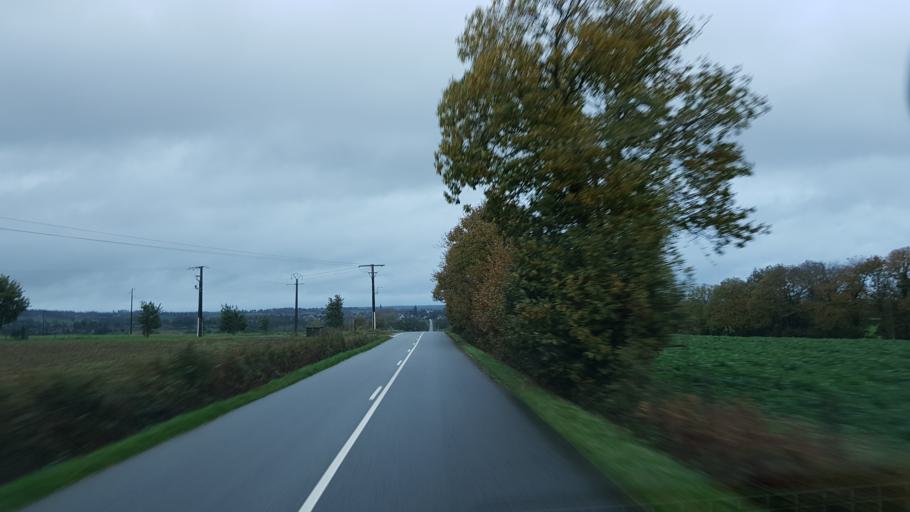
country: FR
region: Brittany
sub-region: Departement d'Ille-et-Vilaine
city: Balaze
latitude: 48.1611
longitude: -1.1360
